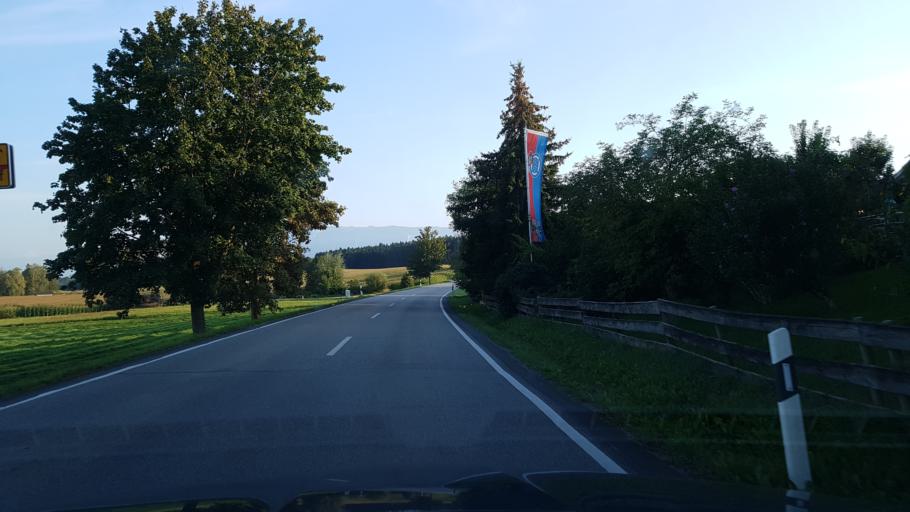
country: DE
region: Bavaria
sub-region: Upper Bavaria
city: Ainring
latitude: 47.8683
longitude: 12.9319
